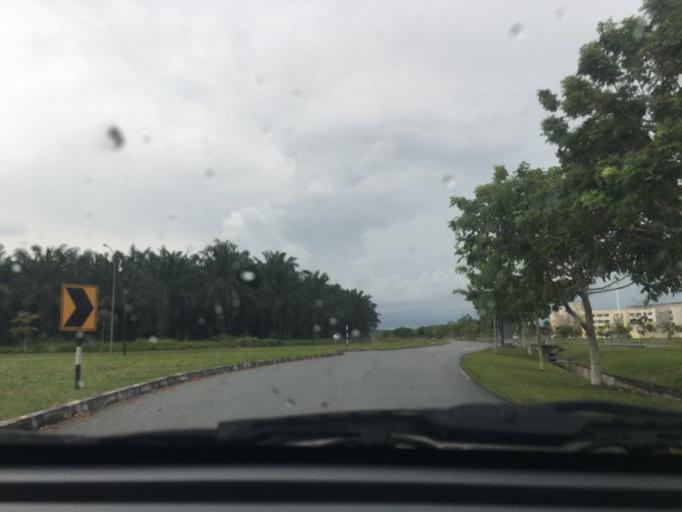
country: MY
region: Kedah
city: Sungai Petani
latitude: 5.5865
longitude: 100.6429
